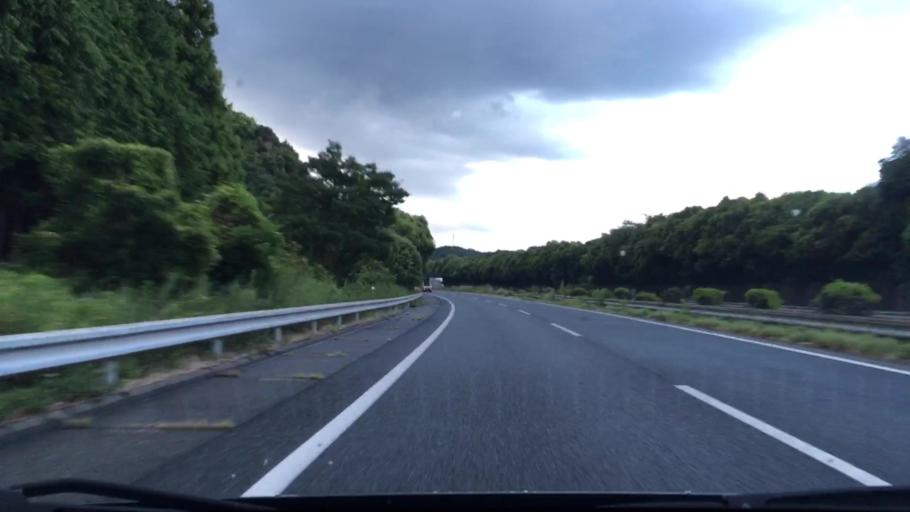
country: JP
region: Yamaguchi
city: Shimonoseki
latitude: 33.8770
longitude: 130.9692
